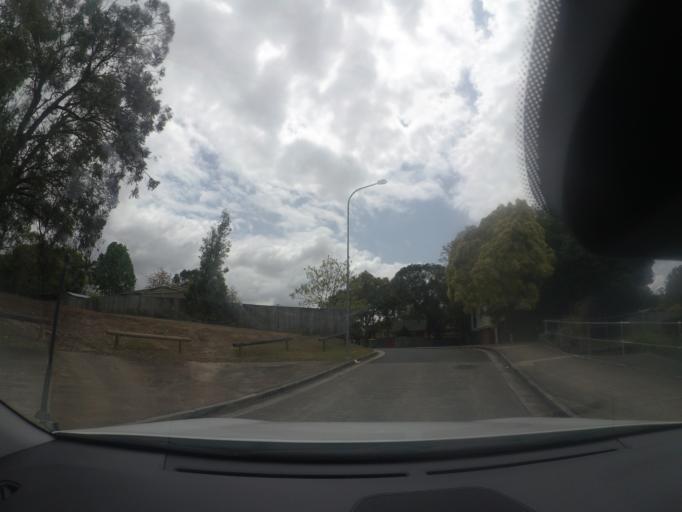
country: AU
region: Queensland
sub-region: Logan
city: Logan City
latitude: -27.6289
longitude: 153.1236
